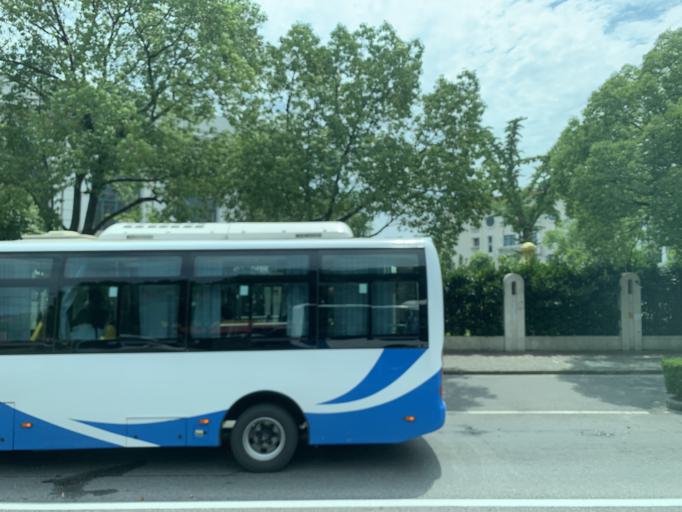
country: CN
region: Shanghai Shi
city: Huamu
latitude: 31.2505
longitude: 121.5792
